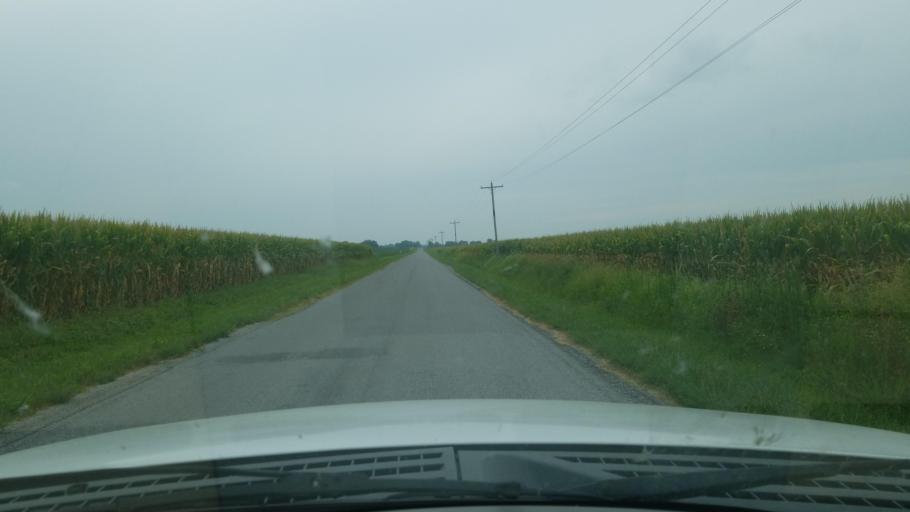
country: US
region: Illinois
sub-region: Saline County
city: Eldorado
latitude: 37.8667
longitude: -88.4692
